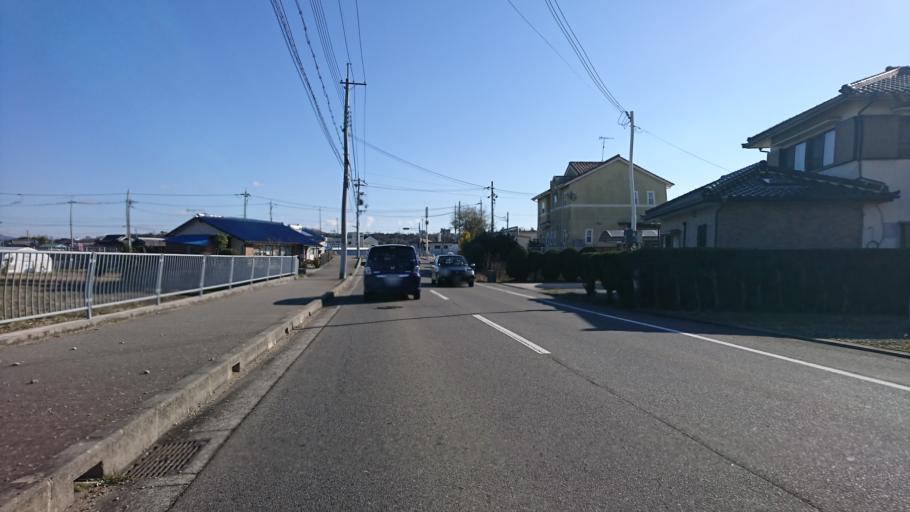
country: JP
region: Hyogo
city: Akashi
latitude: 34.7119
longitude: 134.9819
